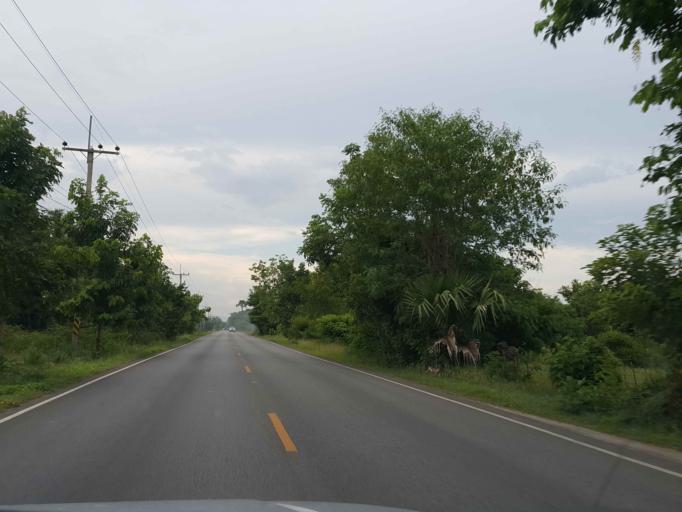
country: TH
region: Lampang
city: Ko Kha
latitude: 18.2369
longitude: 99.3896
